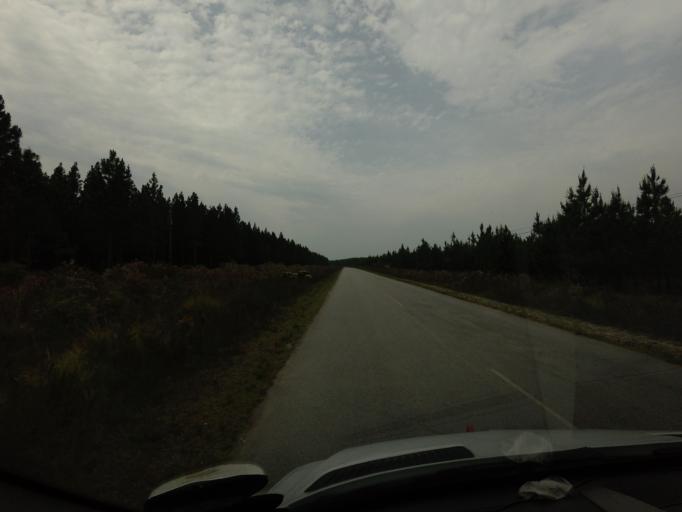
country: ZA
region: Eastern Cape
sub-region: Cacadu District Municipality
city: Kareedouw
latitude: -33.9749
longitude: 23.8401
